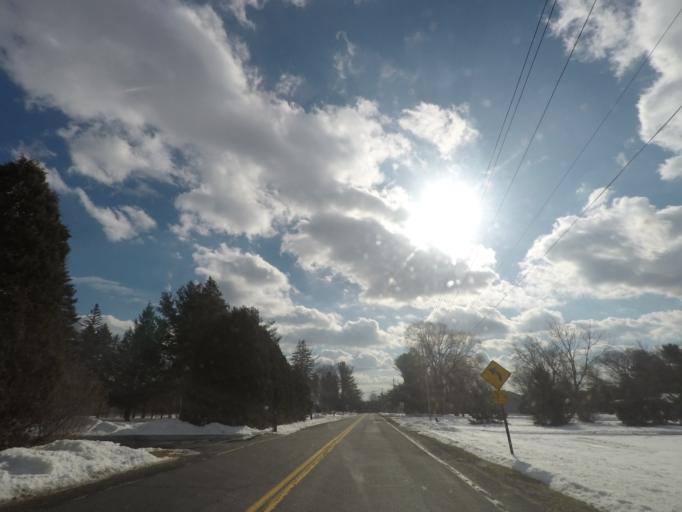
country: US
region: New York
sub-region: Schenectady County
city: Niskayuna
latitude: 42.8300
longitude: -73.8622
